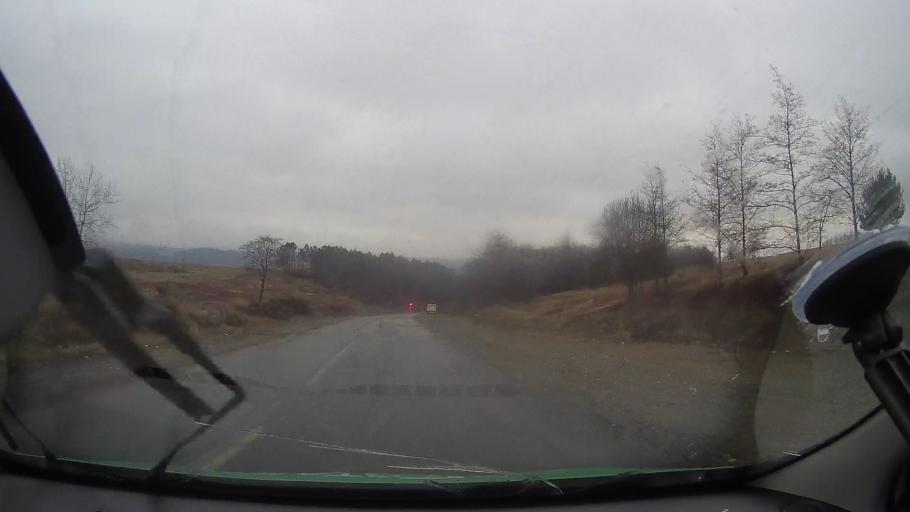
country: RO
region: Arad
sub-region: Comuna Halmagiu
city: Halmagiu
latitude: 46.2810
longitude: 22.5860
